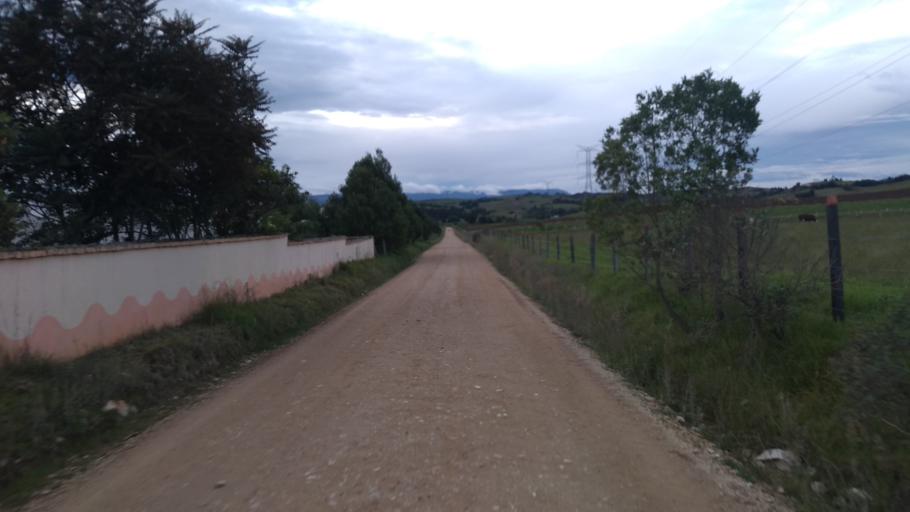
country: CO
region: Boyaca
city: Toca
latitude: 5.6055
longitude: -73.1770
